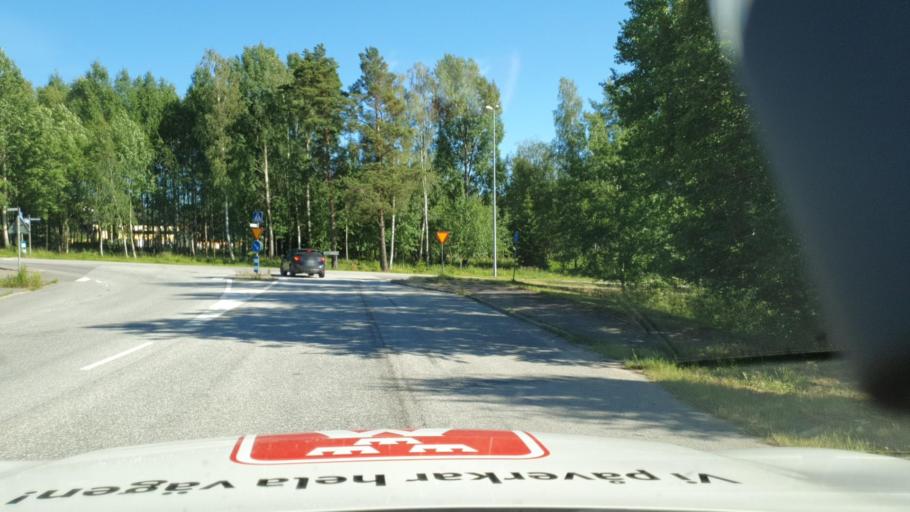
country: SE
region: OErebro
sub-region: Karlskoga Kommun
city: Karlskoga
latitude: 59.3388
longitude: 14.5546
